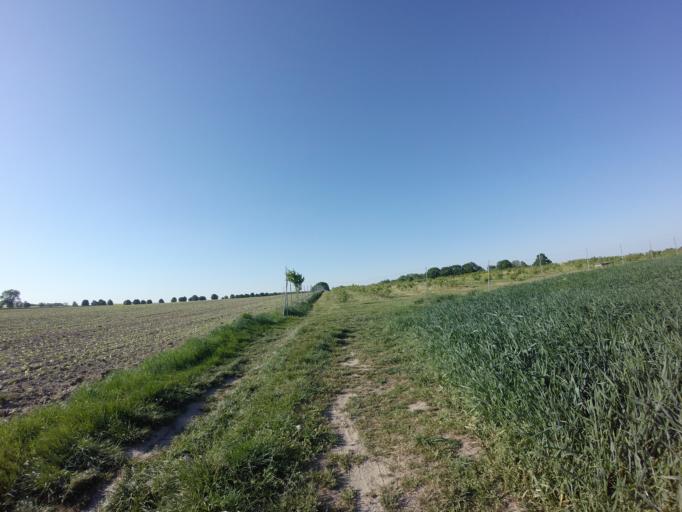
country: PL
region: West Pomeranian Voivodeship
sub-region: Powiat choszczenski
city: Choszczno
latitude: 53.1455
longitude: 15.3860
